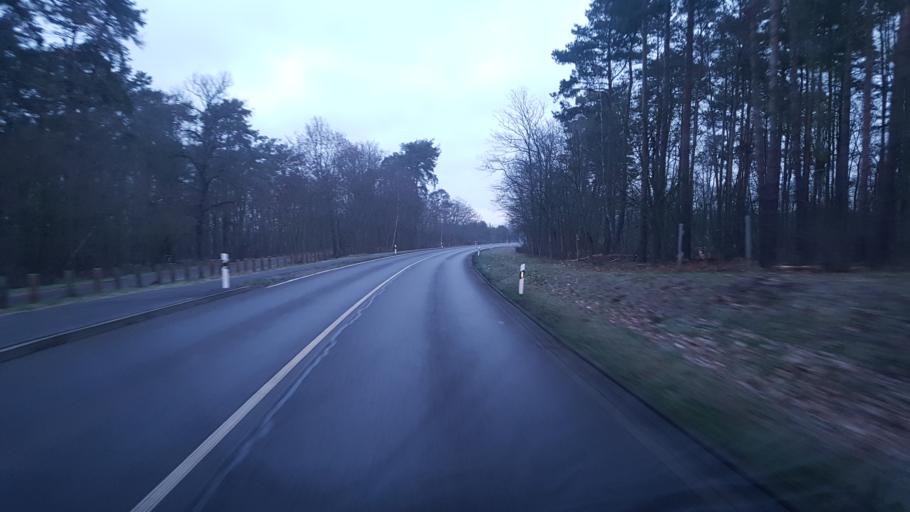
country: DE
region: Brandenburg
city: Ludwigsfelde
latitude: 52.3063
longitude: 13.2060
